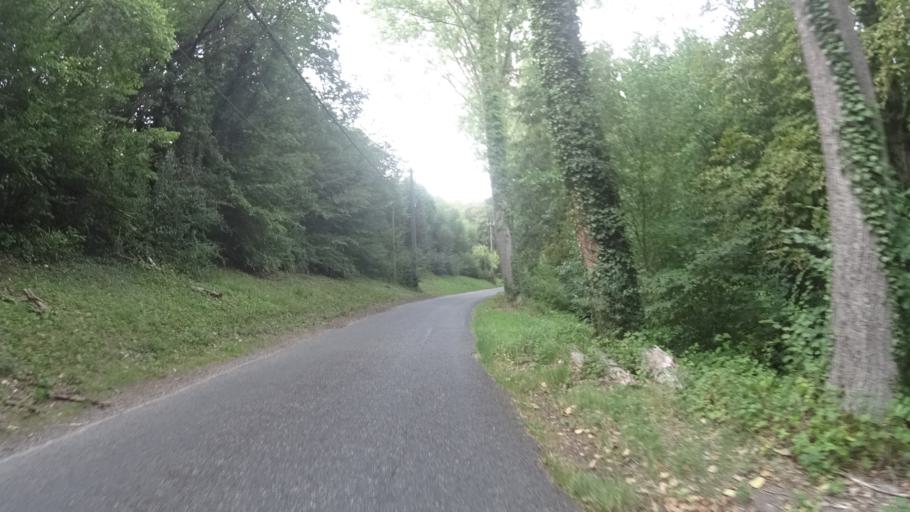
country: FR
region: Picardie
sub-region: Departement de l'Oise
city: Ver-sur-Launette
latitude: 49.1704
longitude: 2.6800
